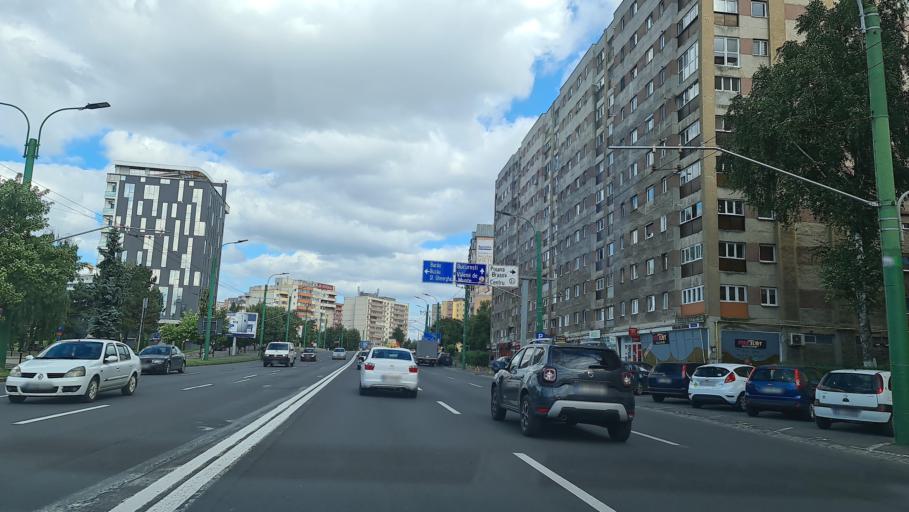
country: RO
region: Brasov
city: Brasov
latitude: 45.6593
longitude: 25.6180
